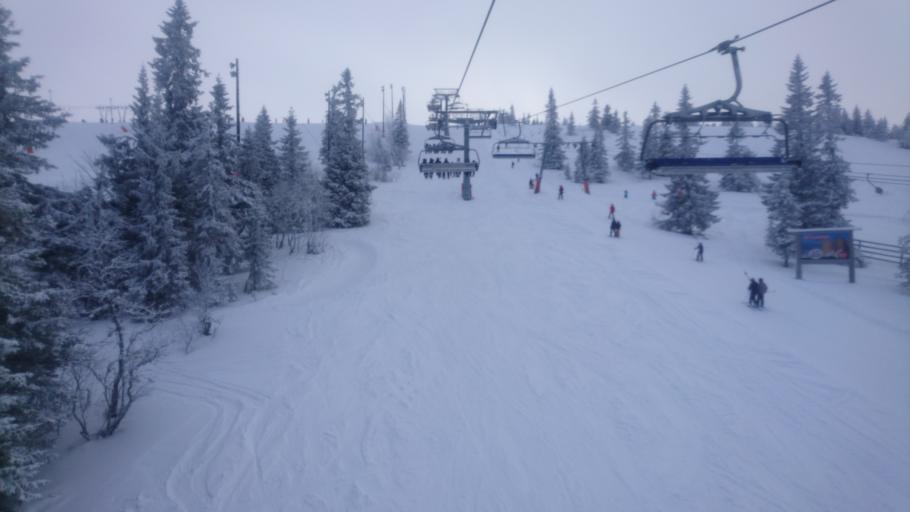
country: SE
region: Dalarna
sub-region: Malung-Saelens kommun
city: Malung
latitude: 61.1568
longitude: 13.1805
